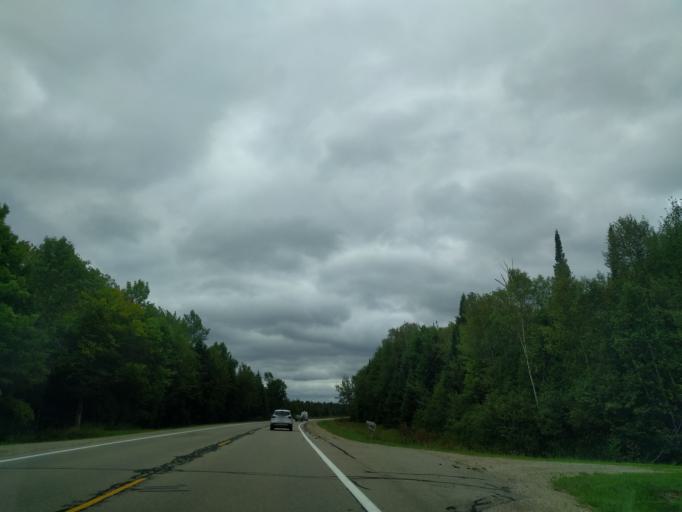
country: US
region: Michigan
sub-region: Menominee County
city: Menominee
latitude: 45.3585
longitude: -87.3999
